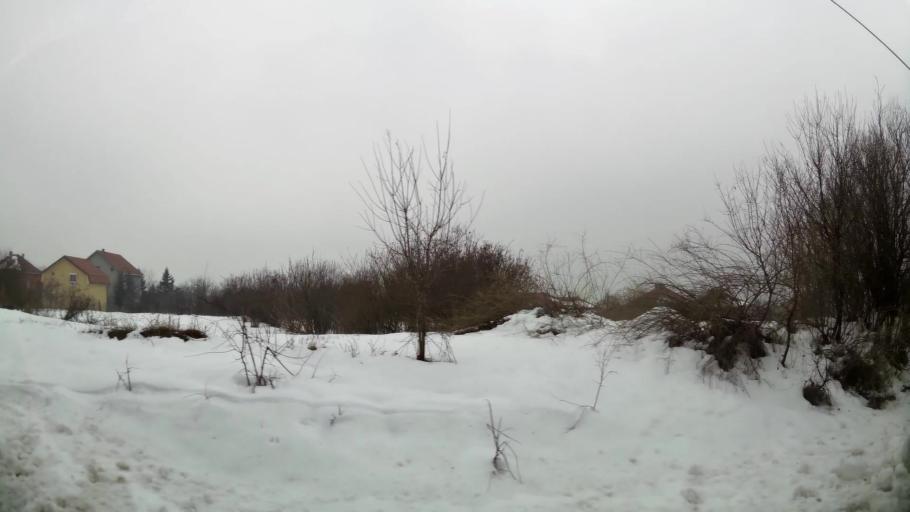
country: RS
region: Central Serbia
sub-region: Belgrade
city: Zvezdara
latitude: 44.7527
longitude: 20.5276
